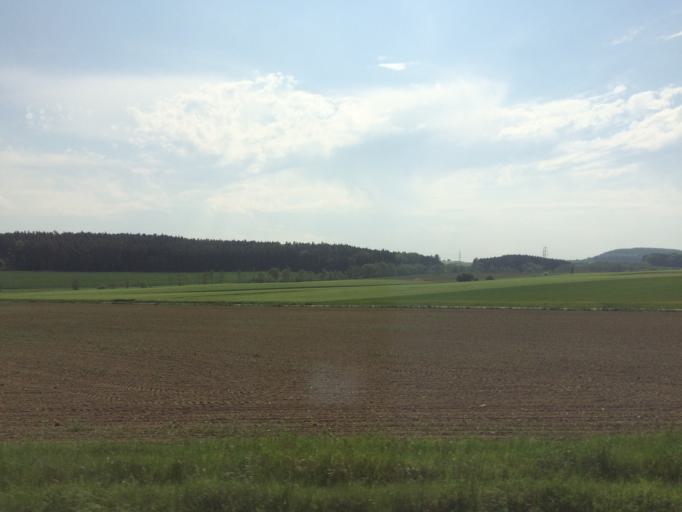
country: DE
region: Bavaria
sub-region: Regierungsbezirk Mittelfranken
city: Baudenbach
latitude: 49.5992
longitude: 10.5448
